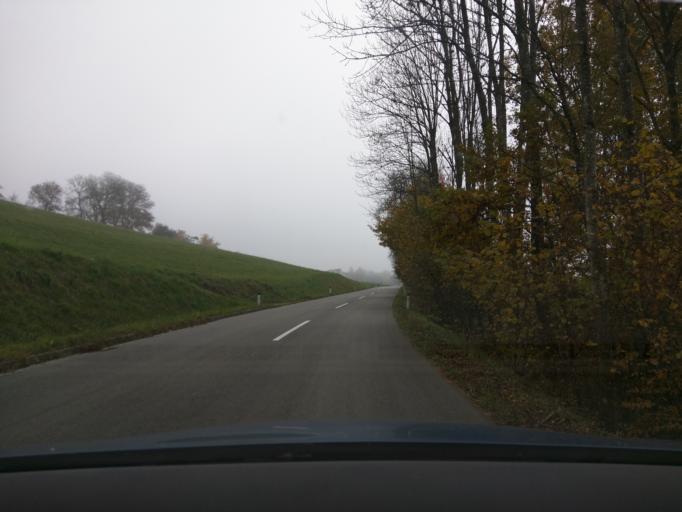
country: DE
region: Bavaria
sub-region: Lower Bavaria
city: Salzweg
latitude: 48.5651
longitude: 13.5034
